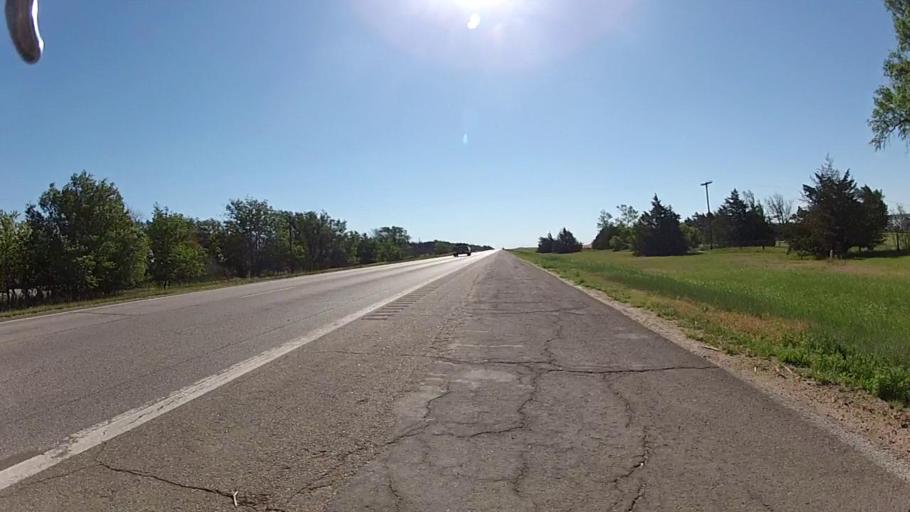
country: US
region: Kansas
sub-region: Kiowa County
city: Greensburg
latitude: 37.5864
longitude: -99.5847
